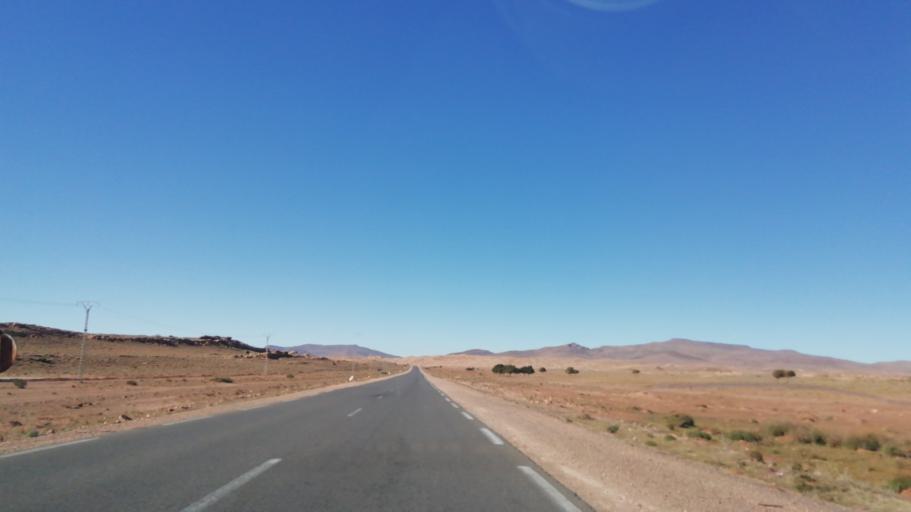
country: DZ
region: El Bayadh
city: El Bayadh
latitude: 33.6155
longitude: 1.2123
